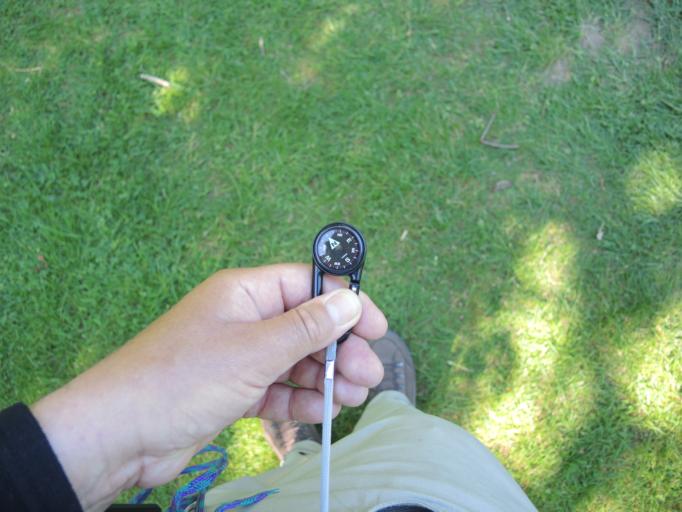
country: BE
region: Flanders
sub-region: Provincie Antwerpen
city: Puurs
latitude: 51.0730
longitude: 4.3102
